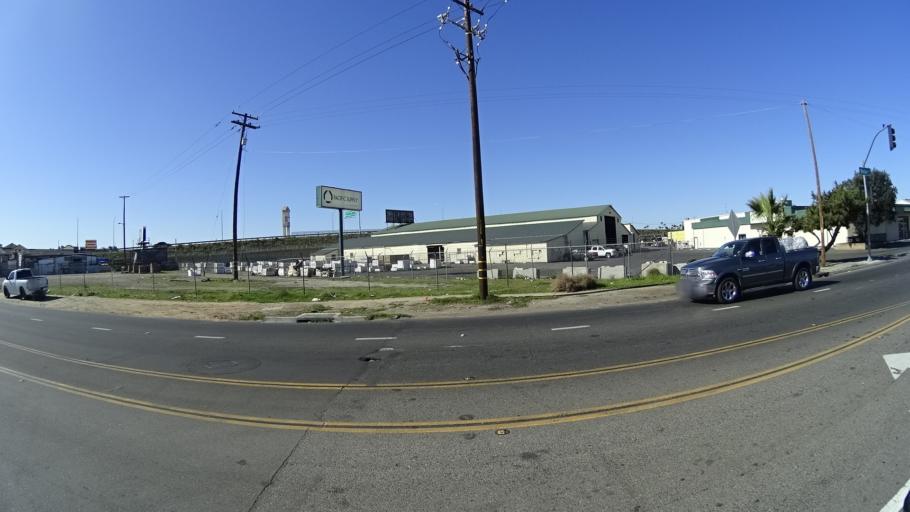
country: US
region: California
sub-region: Fresno County
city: West Park
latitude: 36.7732
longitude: -119.8353
